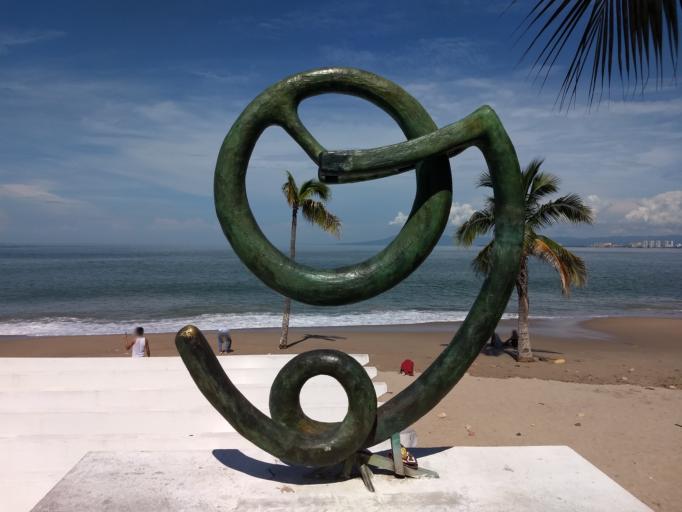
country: MX
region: Jalisco
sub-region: Puerto Vallarta
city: Puerto Vallarta
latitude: 20.6139
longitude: -105.2333
